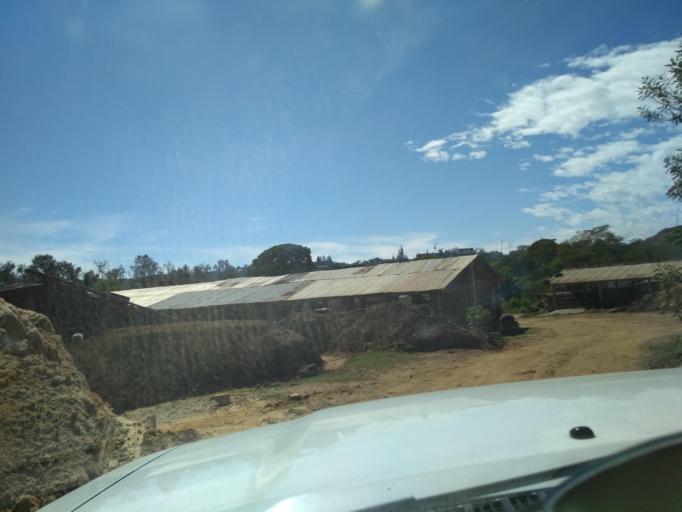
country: MX
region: Veracruz
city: El Castillo
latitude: 19.5469
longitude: -96.8517
